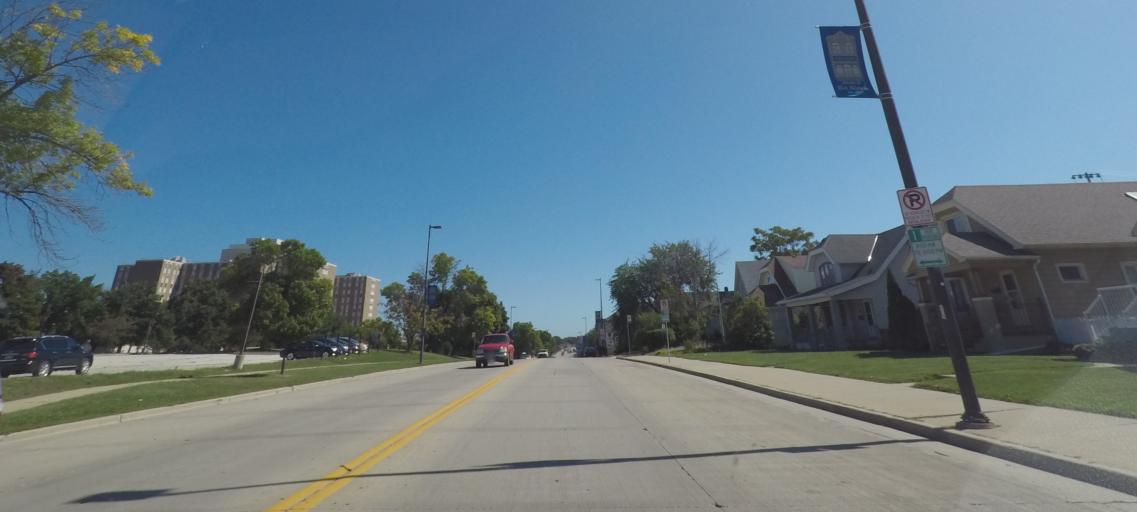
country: US
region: Wisconsin
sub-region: Milwaukee County
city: West Milwaukee
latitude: 43.0191
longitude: -87.9790
